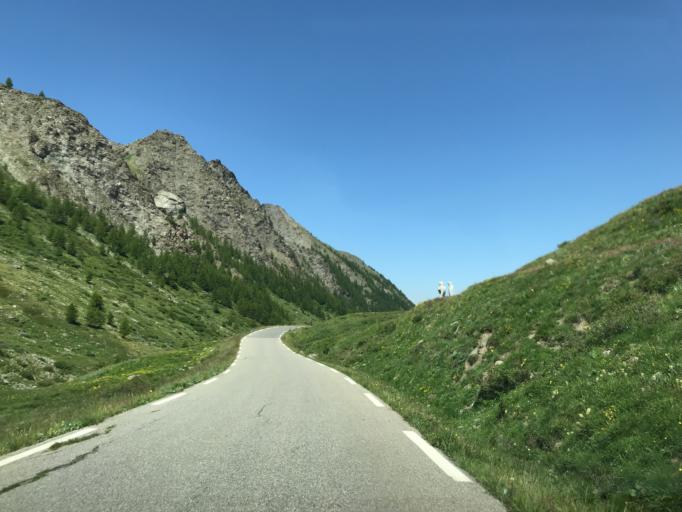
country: IT
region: Piedmont
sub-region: Provincia di Cuneo
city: Pontechianale
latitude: 44.6998
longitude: 6.9431
